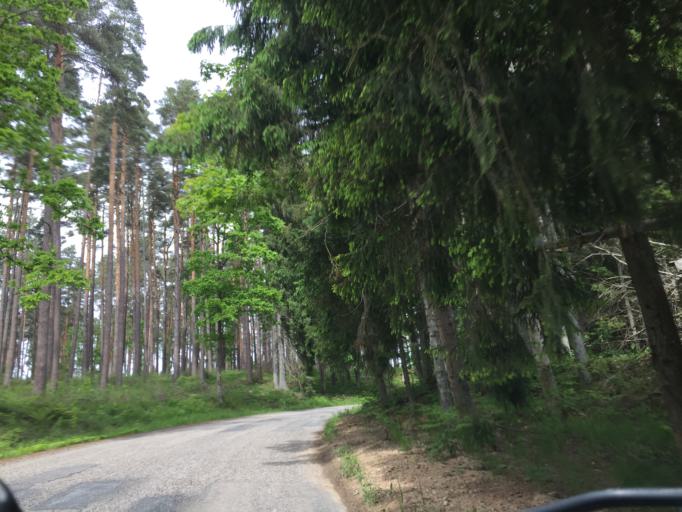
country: LV
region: Koceni
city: Koceni
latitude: 57.5061
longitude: 25.3758
